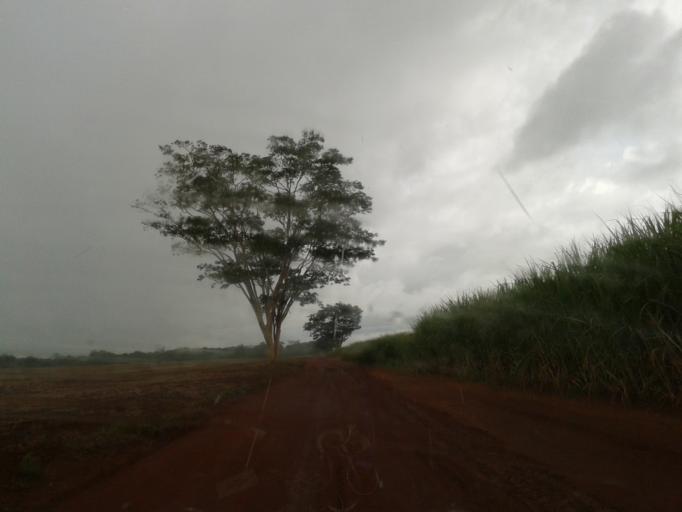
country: BR
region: Minas Gerais
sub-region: Santa Vitoria
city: Santa Vitoria
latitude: -18.6575
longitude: -49.9114
